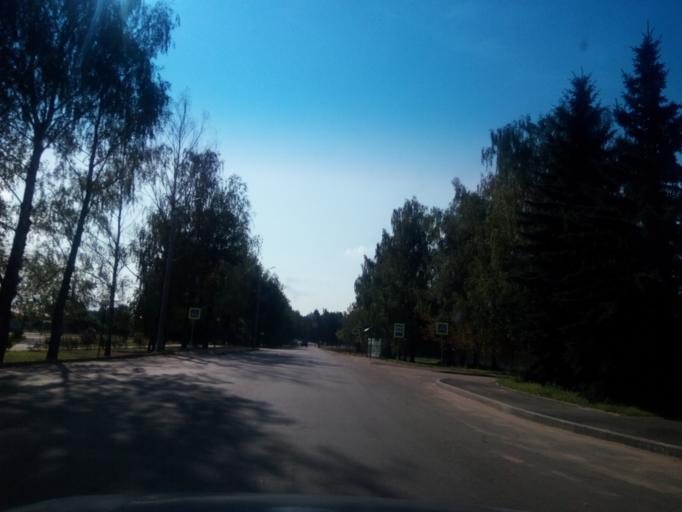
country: BY
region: Vitebsk
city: Vyerkhnyadzvinsk
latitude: 55.7625
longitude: 27.9420
